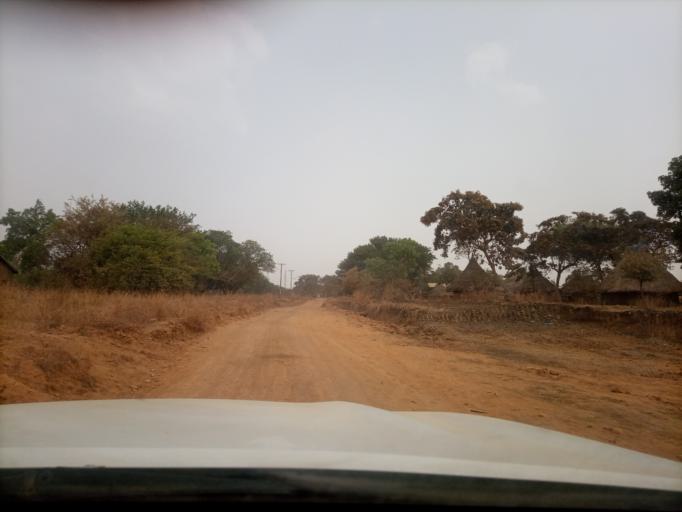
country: ET
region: Oromiya
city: Mendi
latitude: 10.2068
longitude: 35.0875
